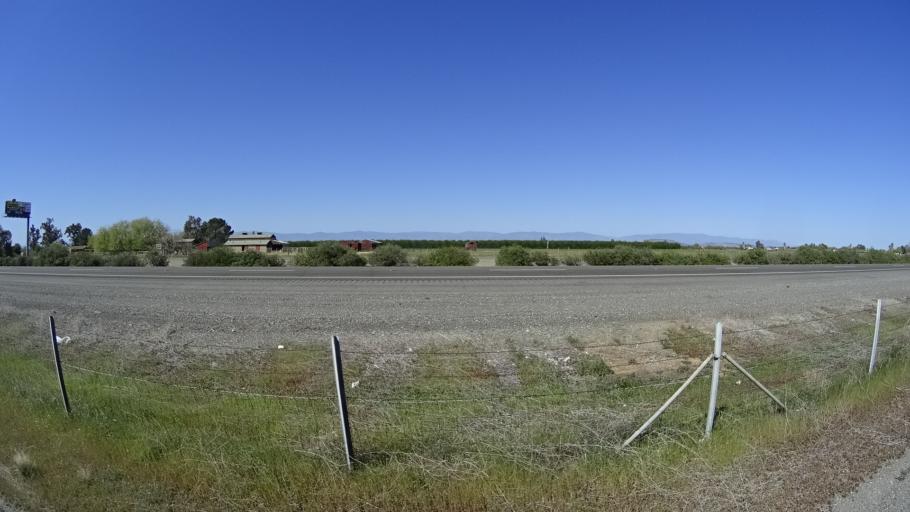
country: US
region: California
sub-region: Glenn County
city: Orland
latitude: 39.6991
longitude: -122.2049
